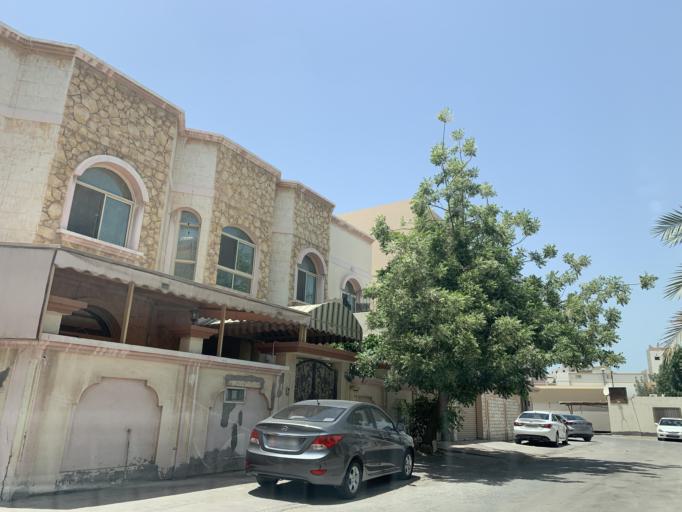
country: BH
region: Northern
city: Sitrah
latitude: 26.1713
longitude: 50.6070
